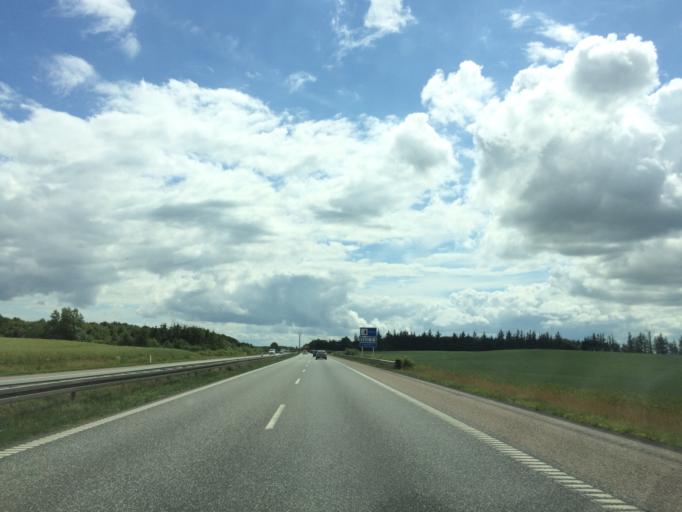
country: DK
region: North Denmark
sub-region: Mariagerfjord Kommune
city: Hobro
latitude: 56.7524
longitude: 9.6956
